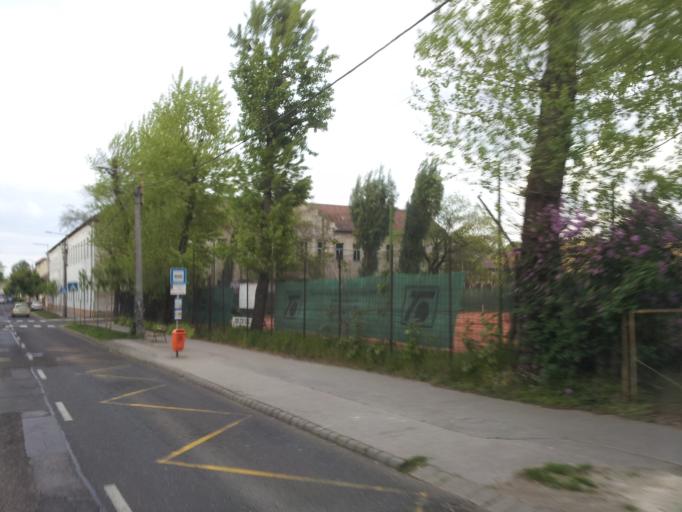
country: HU
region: Budapest
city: Budapest XV. keruelet
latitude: 47.5572
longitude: 19.1135
